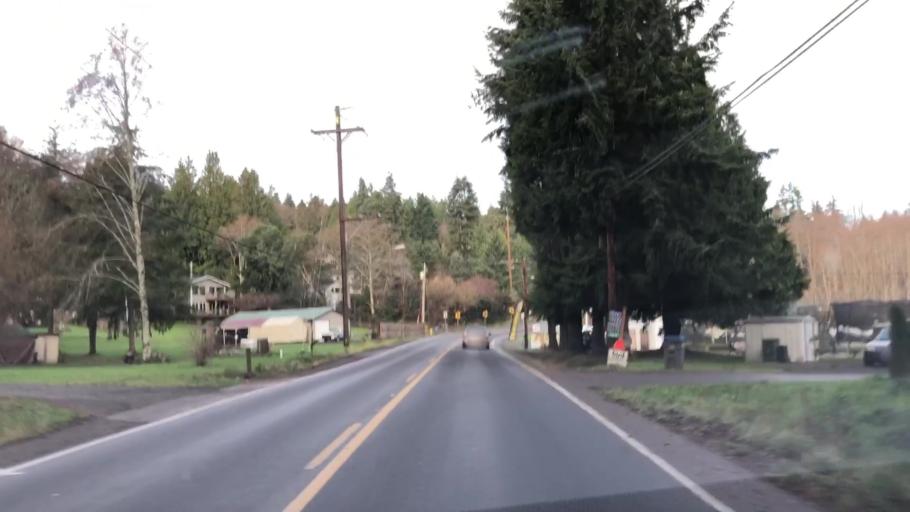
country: US
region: Washington
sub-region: Kitsap County
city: Suquamish
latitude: 47.7481
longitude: -122.5615
